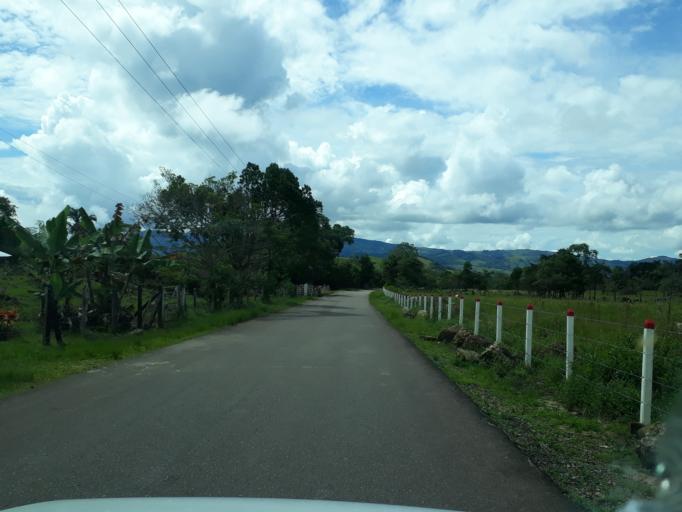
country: CO
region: Cundinamarca
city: Medina
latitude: 4.6422
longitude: -73.3157
